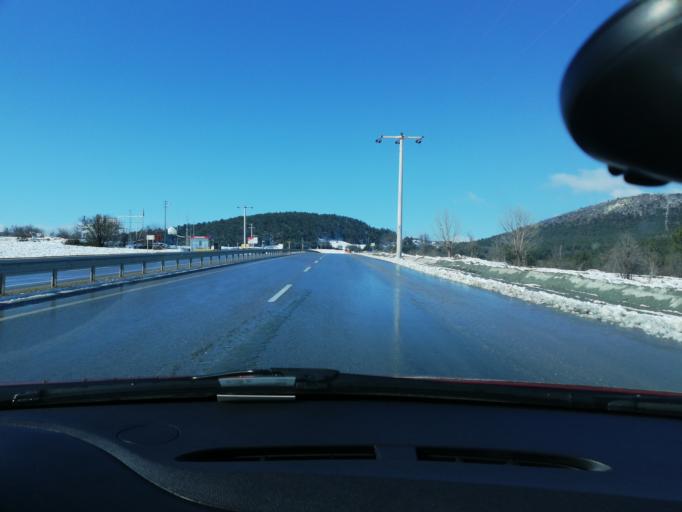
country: TR
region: Kastamonu
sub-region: Cide
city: Kastamonu
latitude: 41.3618
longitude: 33.7113
